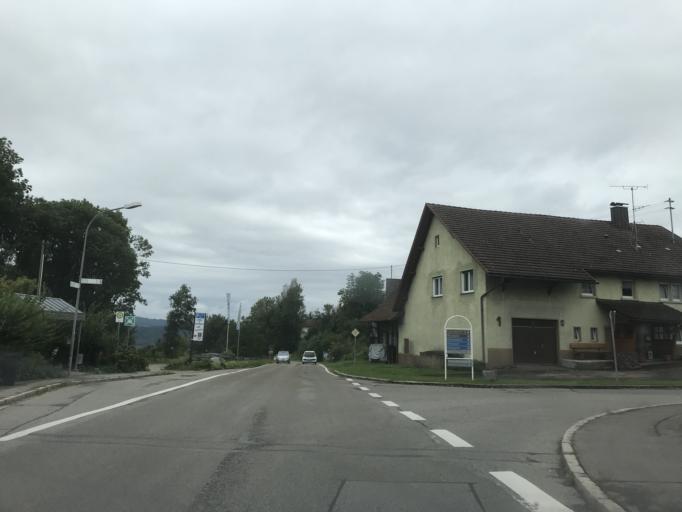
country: DE
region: Baden-Wuerttemberg
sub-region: Freiburg Region
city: Murg
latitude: 47.5824
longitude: 8.0324
